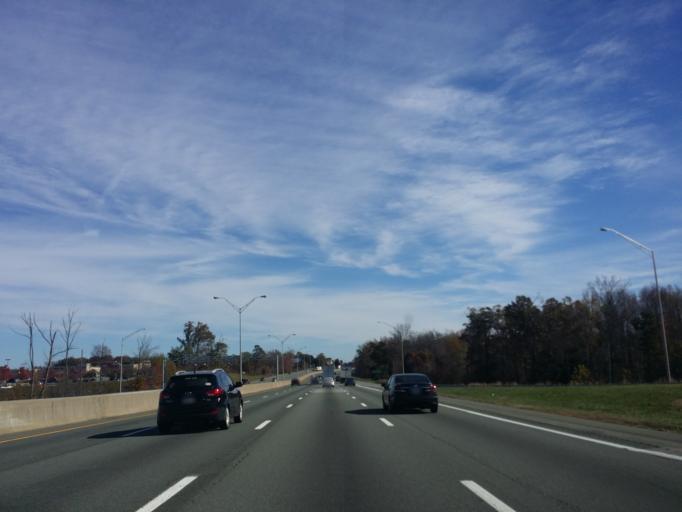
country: US
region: North Carolina
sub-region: Alamance County
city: Elon
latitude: 36.0659
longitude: -79.5131
